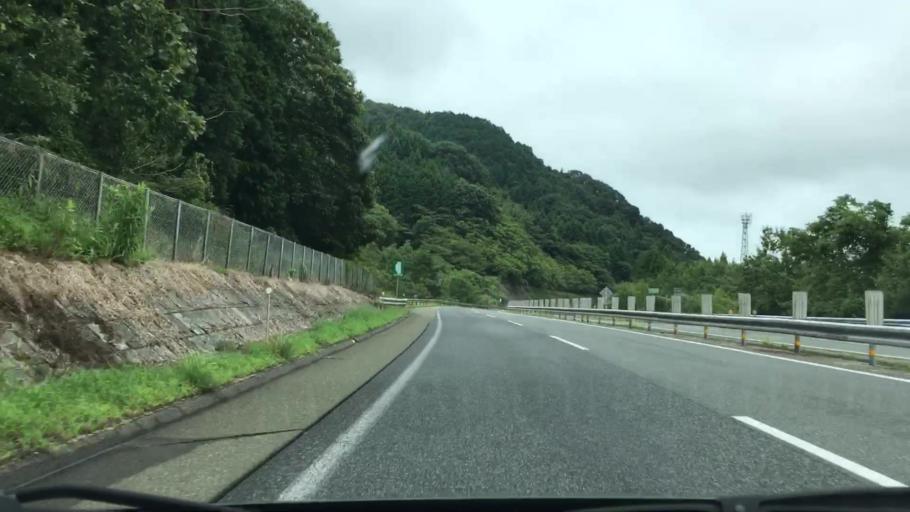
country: JP
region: Hiroshima
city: Shobara
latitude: 34.8452
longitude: 133.0883
